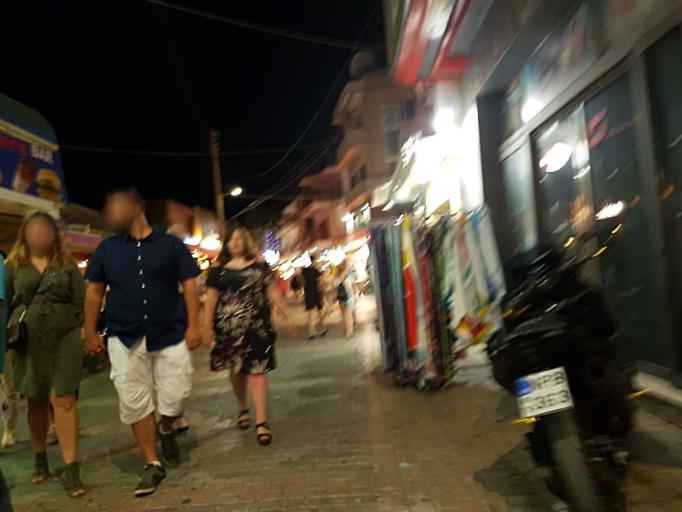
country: GR
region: Crete
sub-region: Nomos Irakleiou
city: Limin Khersonisou
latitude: 35.3190
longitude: 25.3915
